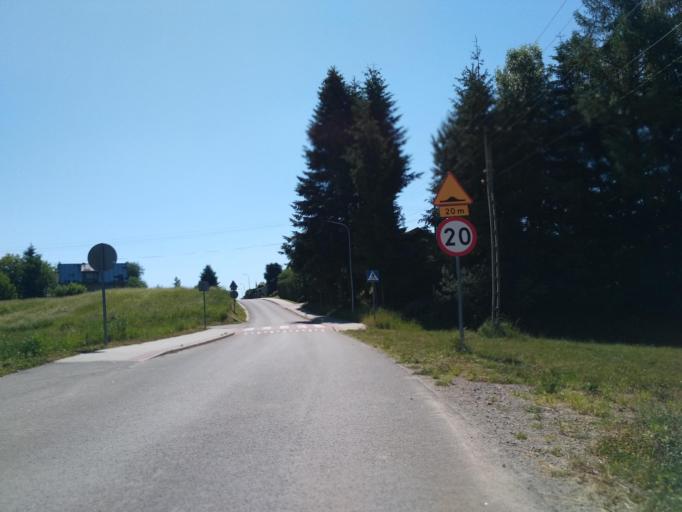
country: PL
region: Subcarpathian Voivodeship
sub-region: Powiat krosnienski
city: Korczyna
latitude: 49.7201
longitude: 21.7991
